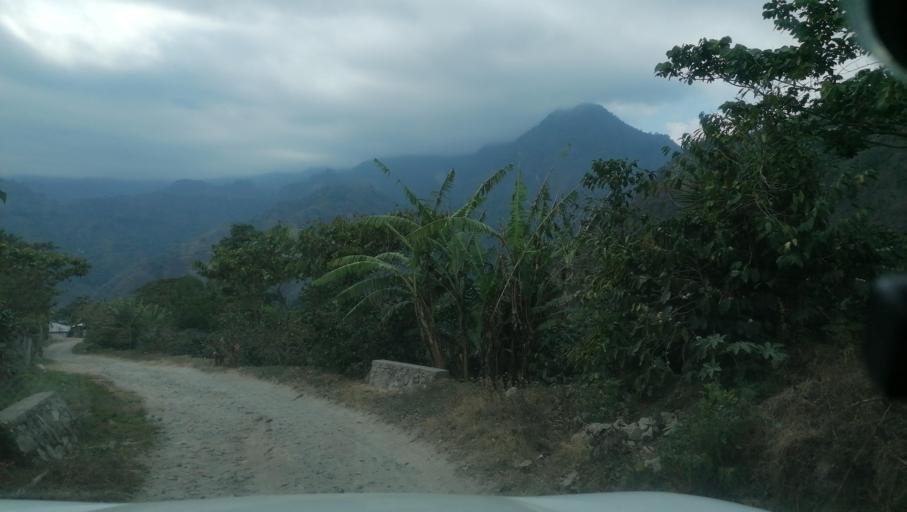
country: MX
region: Chiapas
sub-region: Cacahoatan
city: Benito Juarez
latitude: 15.1702
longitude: -92.1664
